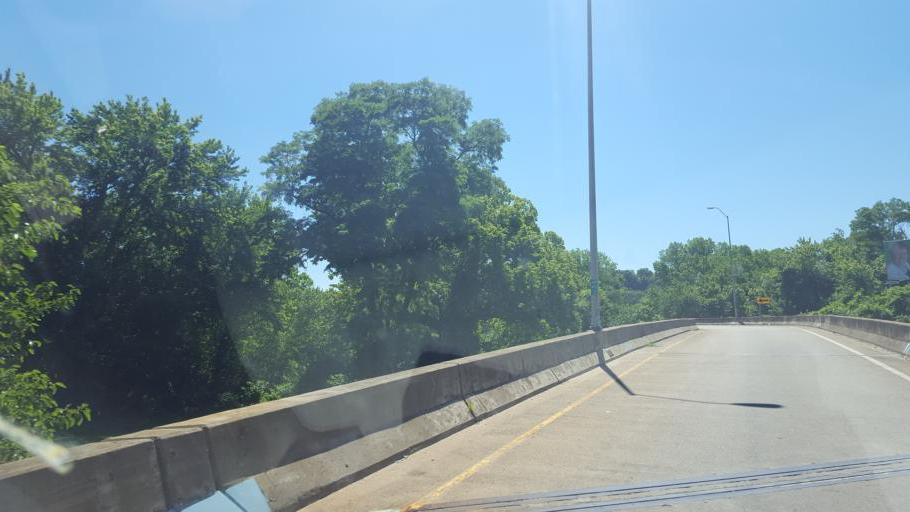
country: US
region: West Virginia
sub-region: Cabell County
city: Huntington
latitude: 38.4278
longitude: -82.3926
